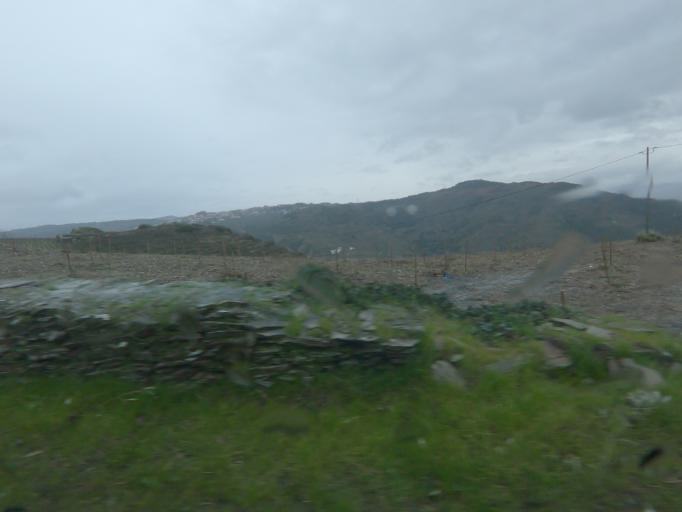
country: PT
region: Viseu
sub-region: Armamar
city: Armamar
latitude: 41.1653
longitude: -7.7027
